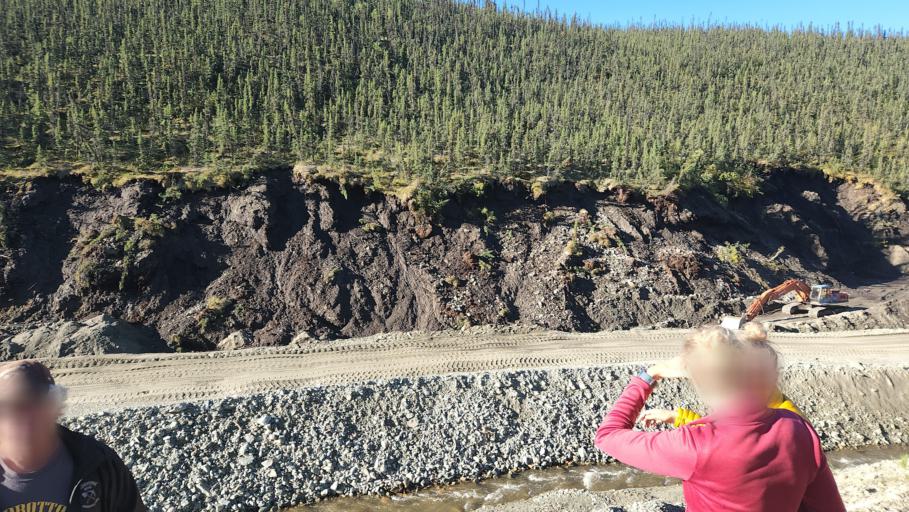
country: CA
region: Yukon
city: Dawson City
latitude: 63.9573
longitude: -138.9364
